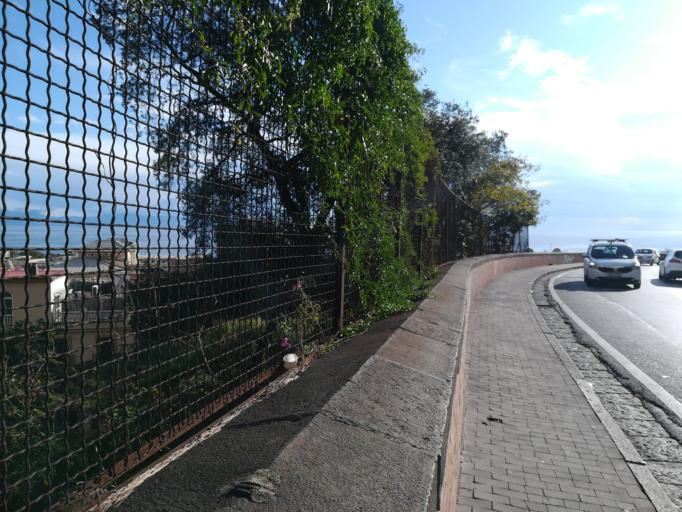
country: IT
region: Campania
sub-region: Provincia di Napoli
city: Napoli
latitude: 40.8378
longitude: 14.2325
